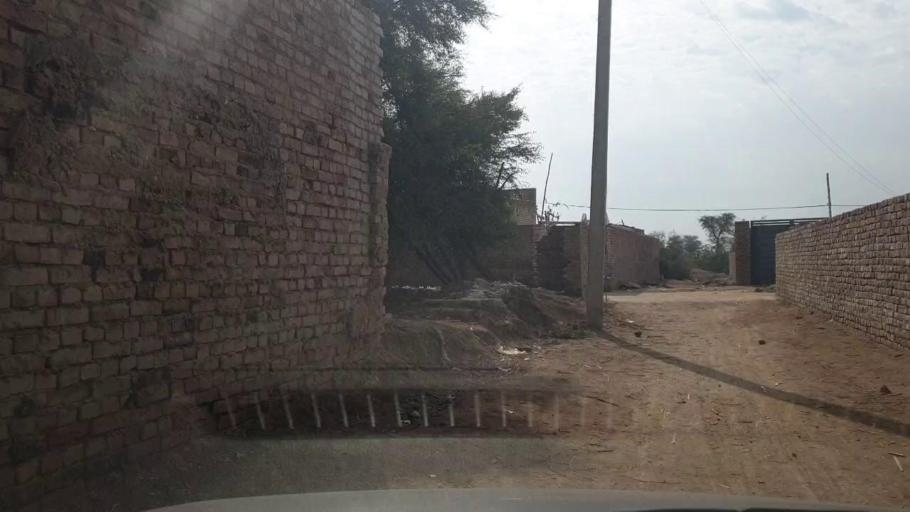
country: PK
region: Sindh
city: Hala
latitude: 25.9998
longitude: 68.4040
